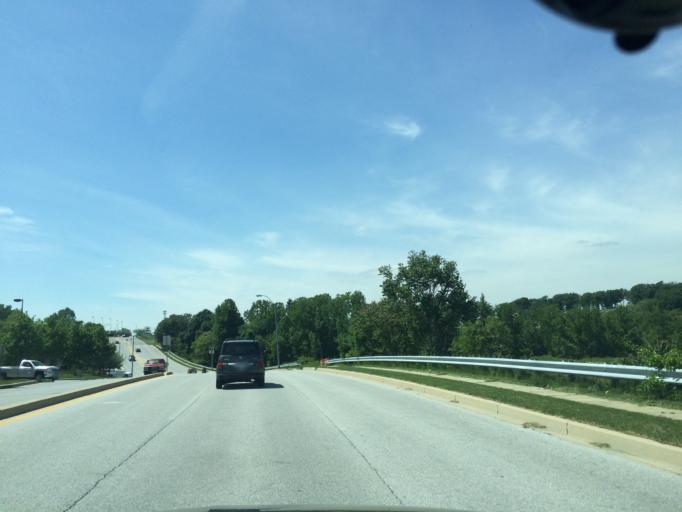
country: US
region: Maryland
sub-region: Carroll County
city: Westminster
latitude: 39.5662
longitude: -76.9690
